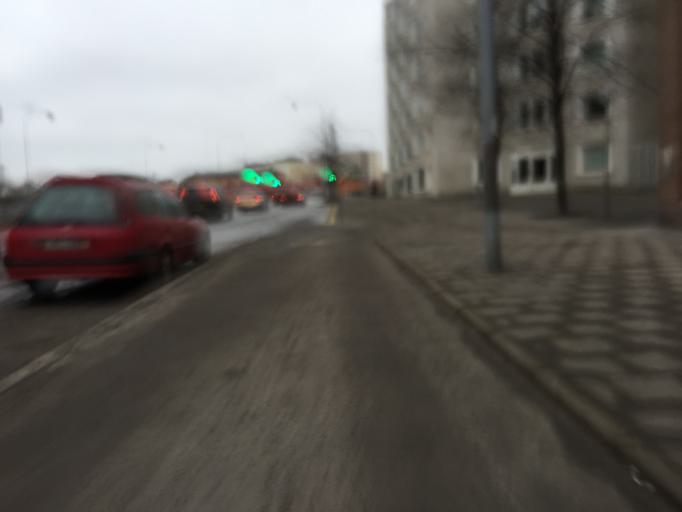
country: SE
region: Stockholm
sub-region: Stockholms Kommun
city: Stockholm
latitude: 59.3337
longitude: 18.0459
